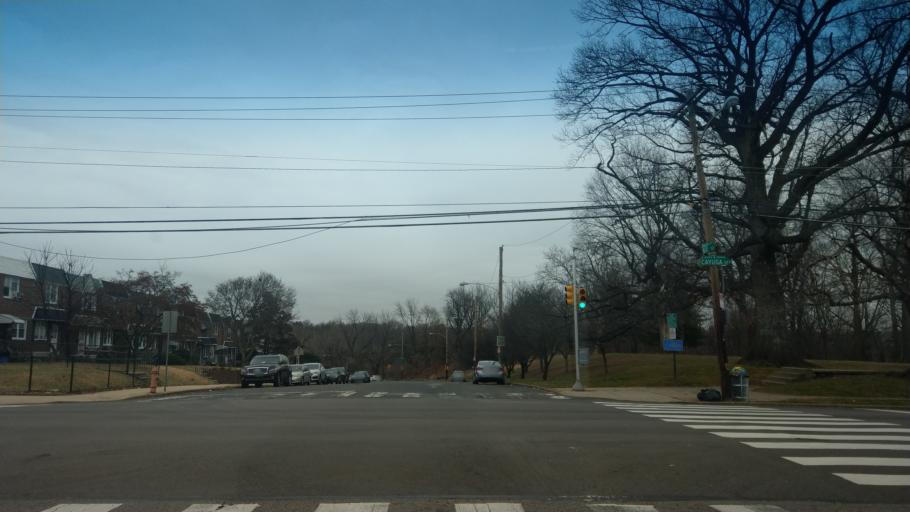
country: US
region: Pennsylvania
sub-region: Montgomery County
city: Rockledge
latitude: 40.0145
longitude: -75.1074
